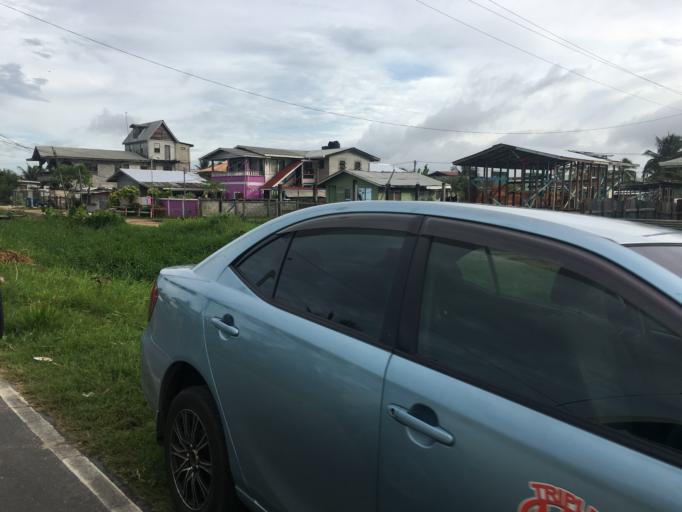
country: GY
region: Demerara-Mahaica
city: Georgetown
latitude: 6.8032
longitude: -58.1250
